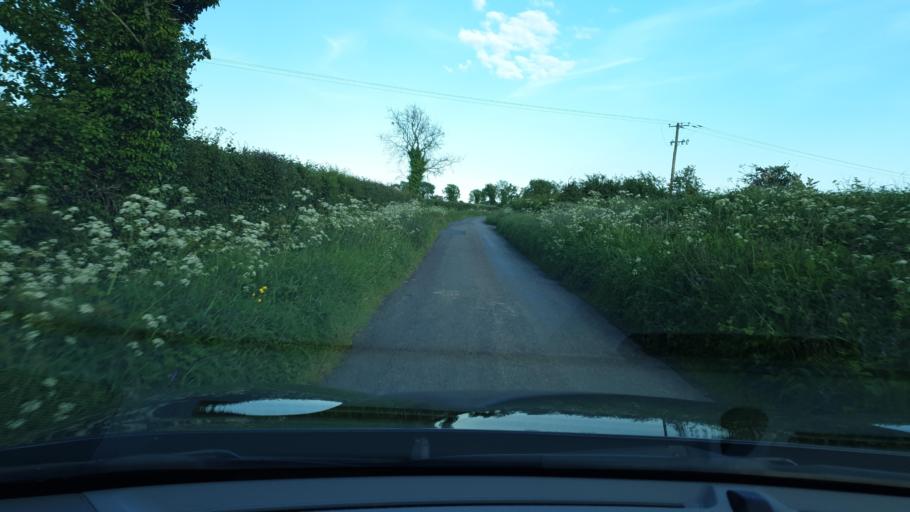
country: IE
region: Leinster
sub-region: An Mhi
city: Ashbourne
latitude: 53.5541
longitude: -6.3626
